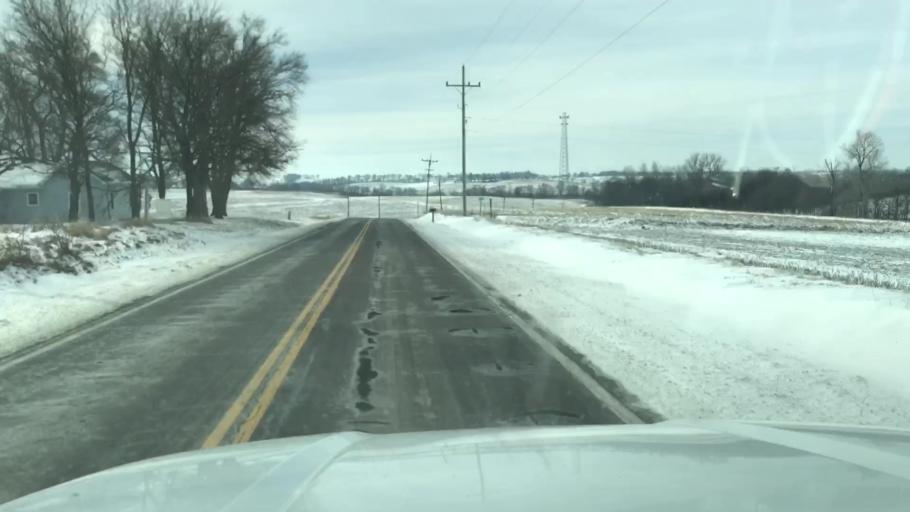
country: US
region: Missouri
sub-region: Holt County
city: Oregon
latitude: 40.0511
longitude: -95.1358
